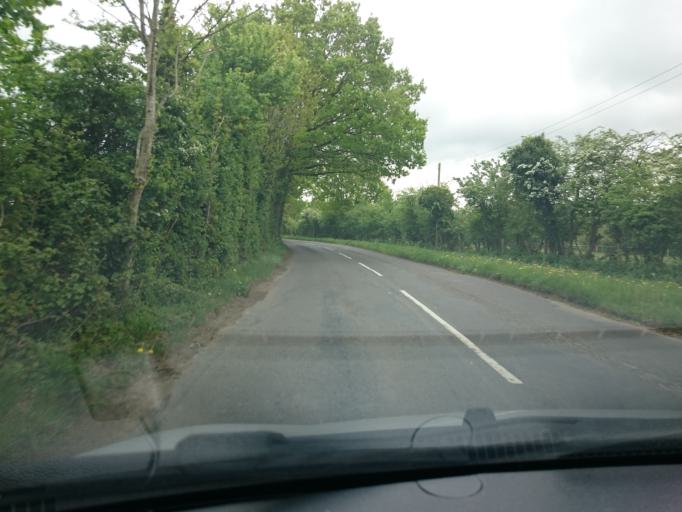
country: GB
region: England
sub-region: Surrey
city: Seale
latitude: 51.2438
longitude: -0.7129
